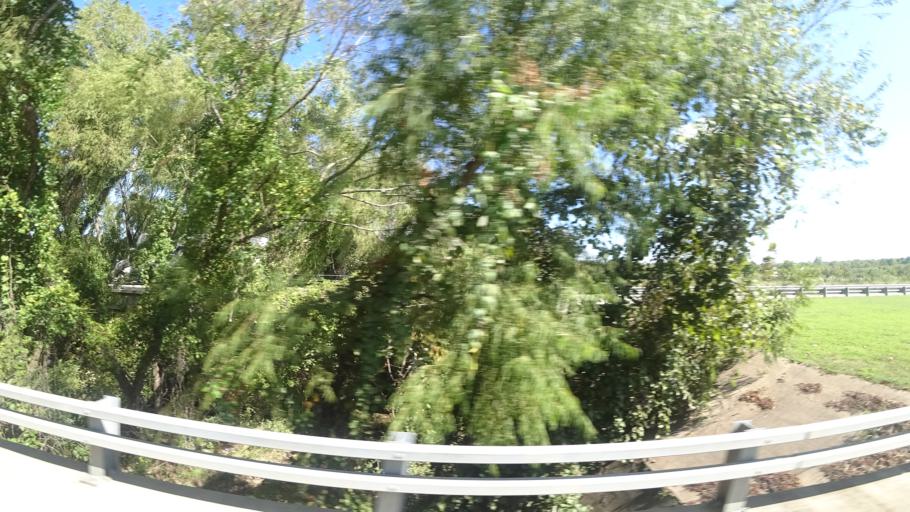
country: US
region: Texas
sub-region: Travis County
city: Manor
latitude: 30.3632
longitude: -97.6138
